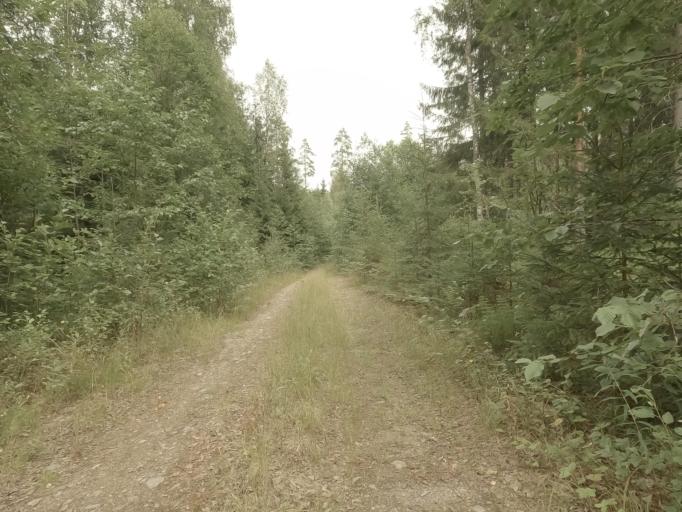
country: RU
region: Leningrad
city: Kamennogorsk
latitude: 61.0188
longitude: 29.1613
